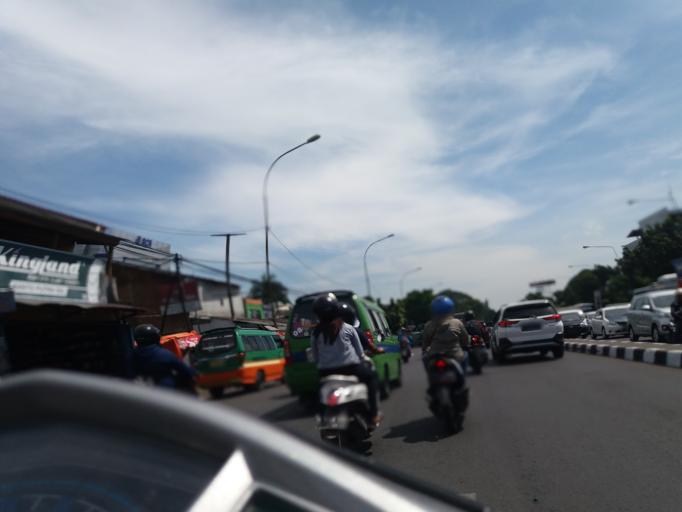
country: ID
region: West Java
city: Margahayukencana
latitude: -6.9473
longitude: 107.5950
